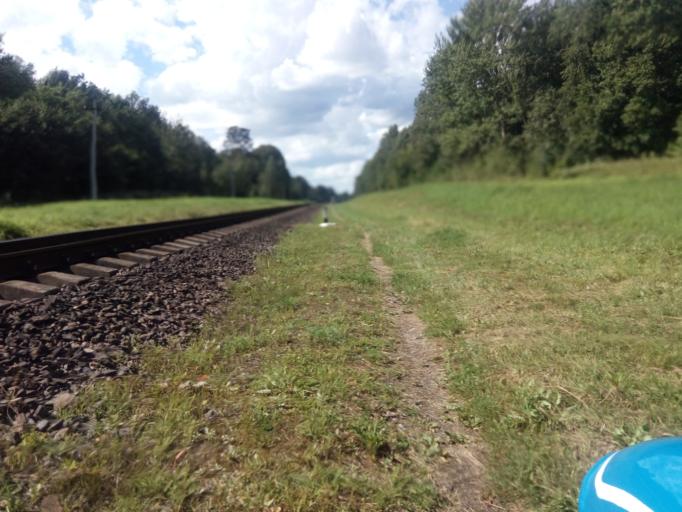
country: BY
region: Vitebsk
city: Dzisna
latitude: 55.6775
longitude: 28.3025
